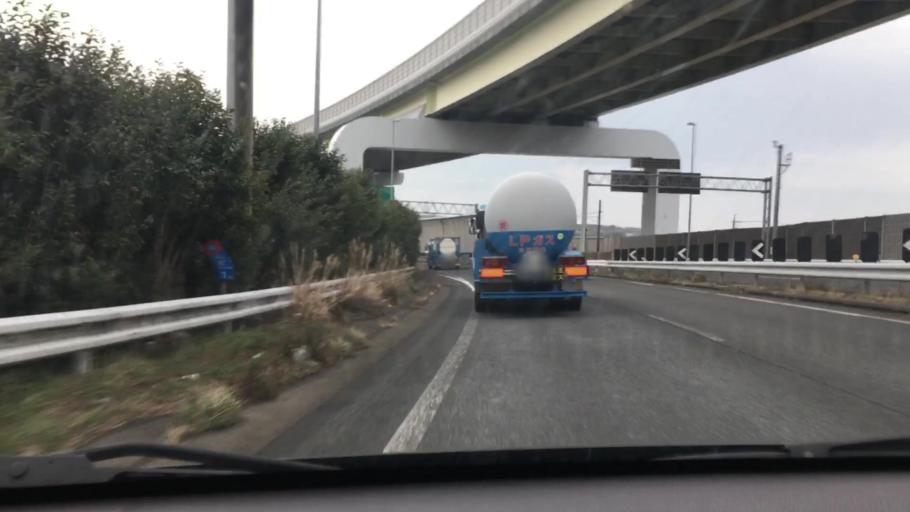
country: JP
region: Mie
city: Kameyama
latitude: 34.8498
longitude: 136.4164
